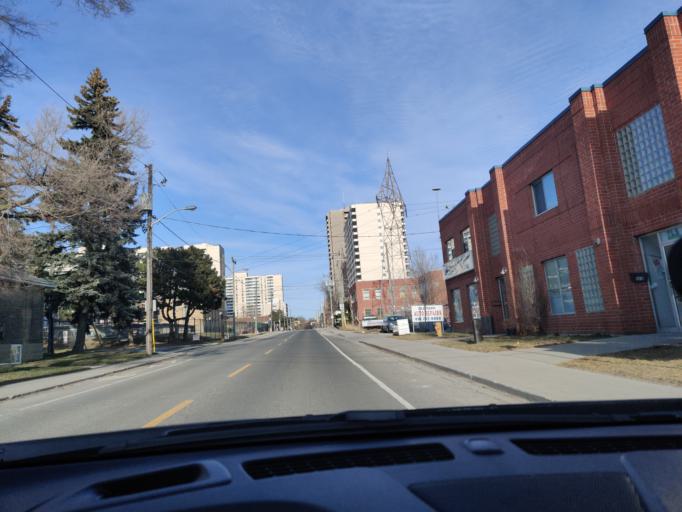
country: CA
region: Ontario
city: Toronto
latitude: 43.7016
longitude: -79.4442
